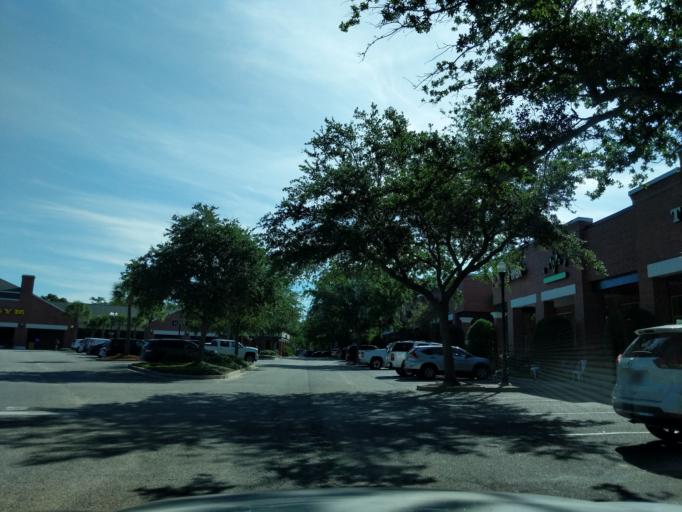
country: US
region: South Carolina
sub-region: Charleston County
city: Mount Pleasant
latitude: 32.7929
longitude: -79.8691
